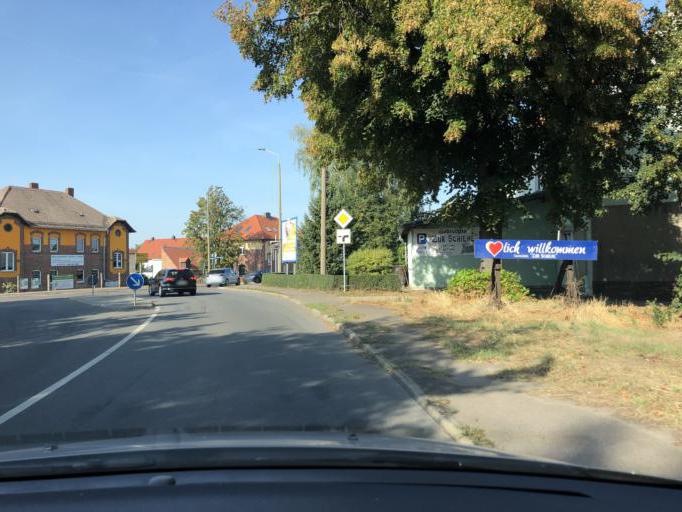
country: DE
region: Saxony-Anhalt
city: Zscherben
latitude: 51.3233
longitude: 11.9628
